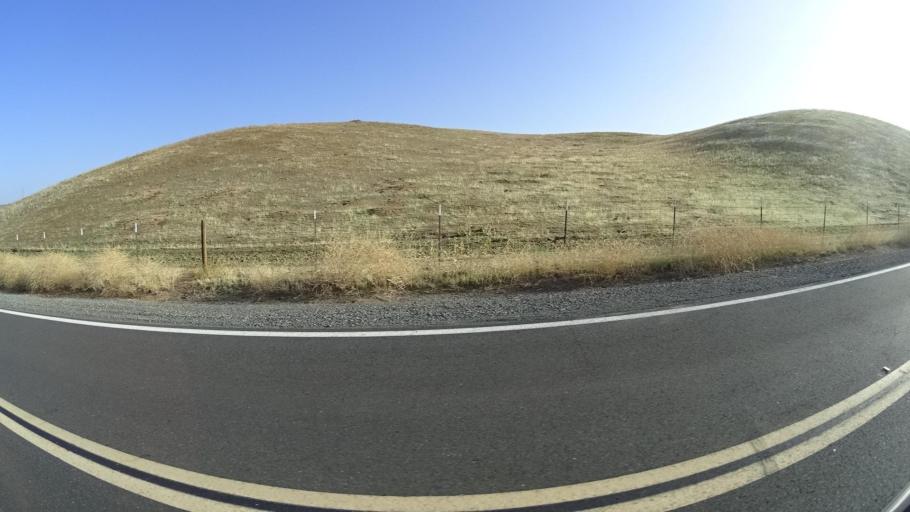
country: US
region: California
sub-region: Tulare County
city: Richgrove
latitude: 35.7434
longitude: -118.8785
